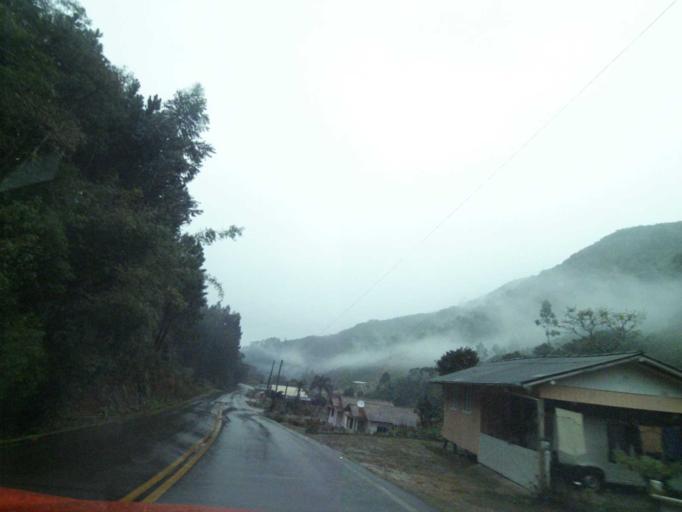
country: BR
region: Santa Catarina
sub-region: Anitapolis
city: Anitapolis
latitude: -27.8301
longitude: -49.0511
